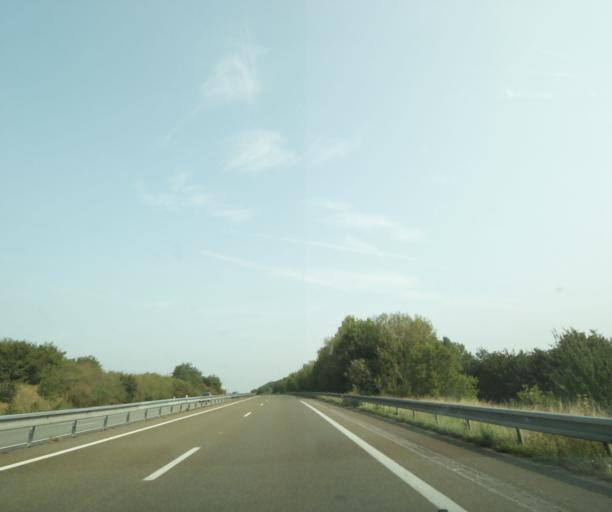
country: FR
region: Pays de la Loire
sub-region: Departement de la Sarthe
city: Neuville-sur-Sarthe
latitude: 48.0891
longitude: 0.1765
